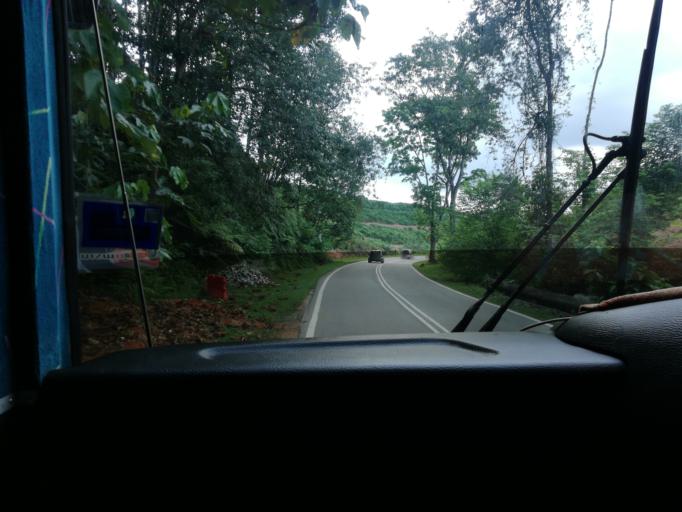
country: MY
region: Kedah
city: Kulim
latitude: 5.3057
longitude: 100.6157
